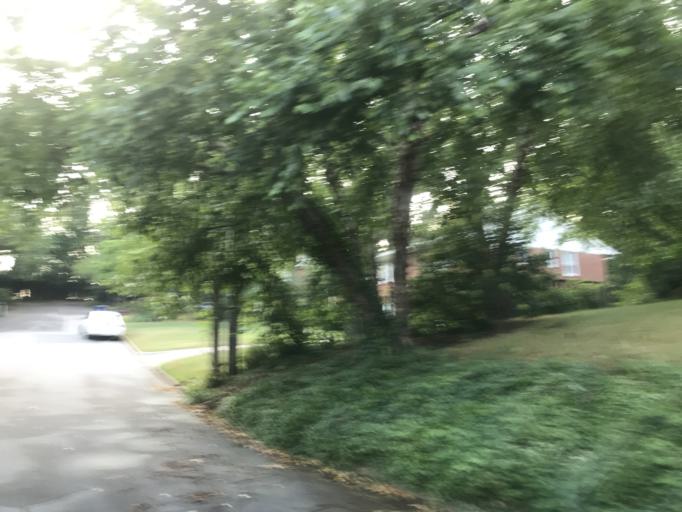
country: US
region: North Carolina
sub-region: Wake County
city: West Raleigh
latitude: 35.8001
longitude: -78.6563
